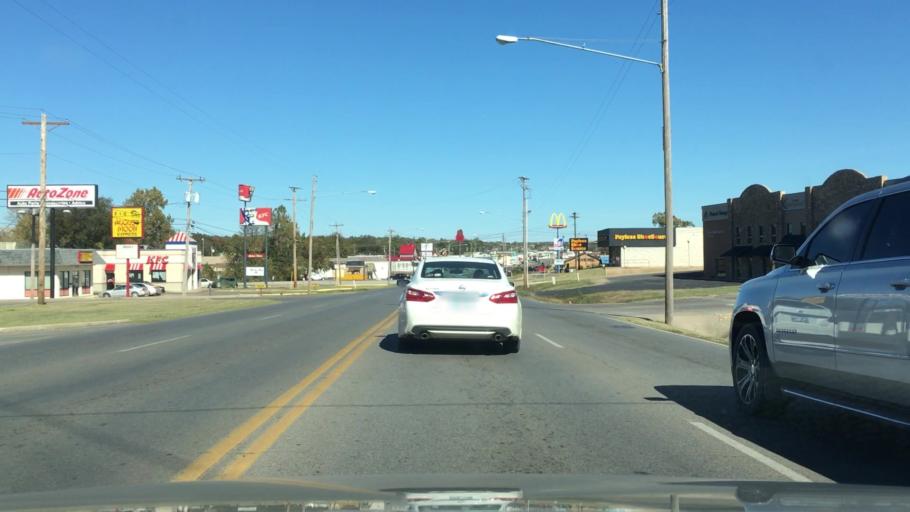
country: US
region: Oklahoma
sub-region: Cherokee County
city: Tahlequah
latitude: 35.8939
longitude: -94.9771
